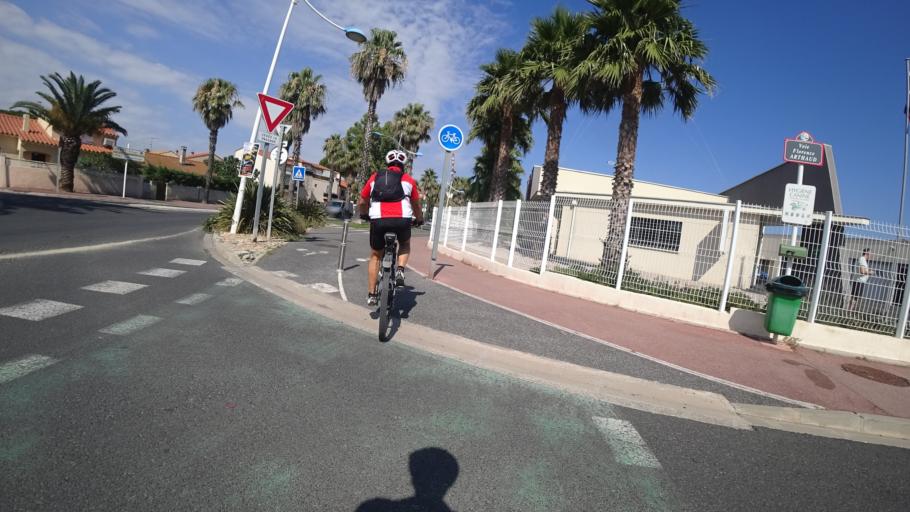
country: FR
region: Languedoc-Roussillon
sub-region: Departement des Pyrenees-Orientales
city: Canet-en-Roussillon
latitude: 42.7017
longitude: 3.0300
